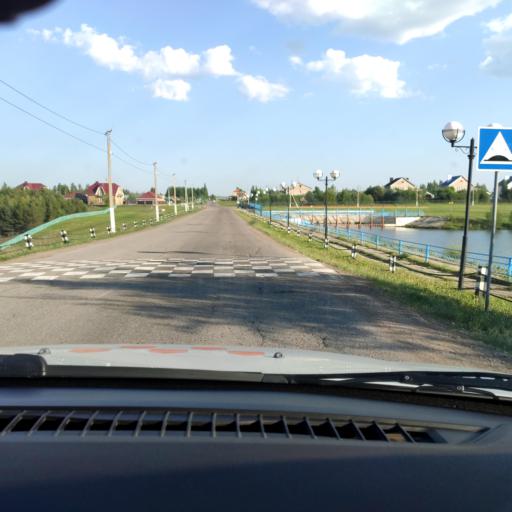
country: RU
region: Bashkortostan
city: Karmaskaly
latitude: 54.3718
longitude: 56.1529
